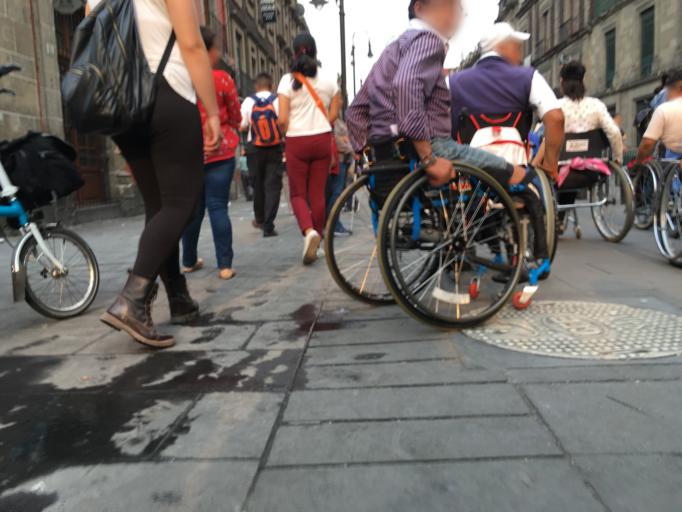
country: MX
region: Mexico City
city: Mexico City
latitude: 19.4335
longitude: -99.1309
